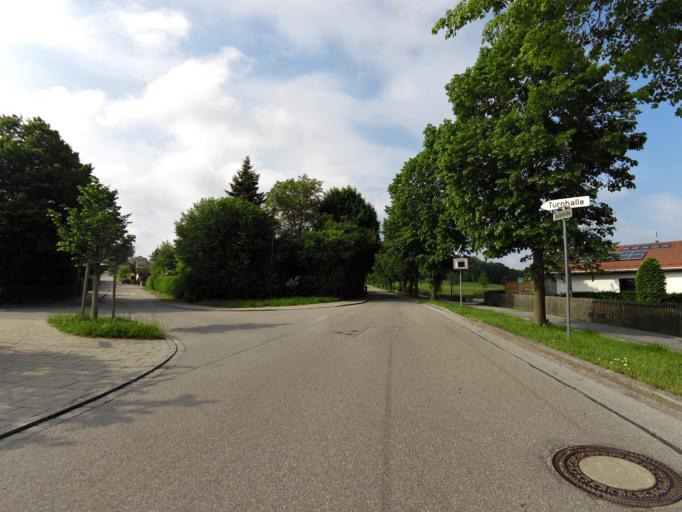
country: DE
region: Bavaria
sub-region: Upper Bavaria
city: Schaftlarn
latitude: 47.9861
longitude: 11.4547
